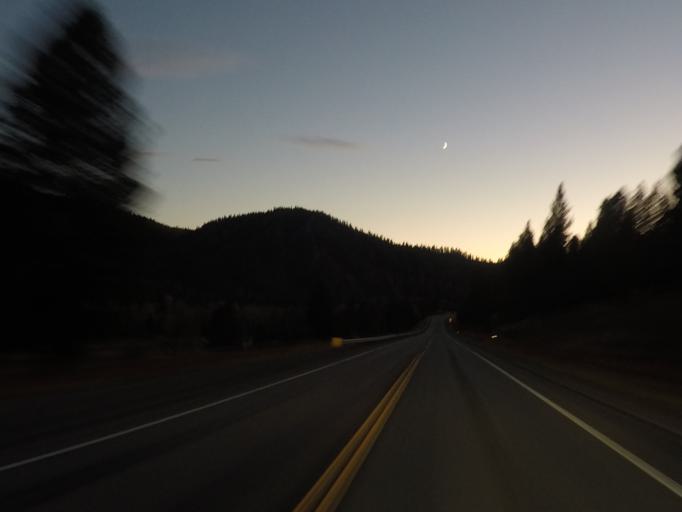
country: US
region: Montana
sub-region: Missoula County
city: Seeley Lake
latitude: 47.0270
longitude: -113.2865
